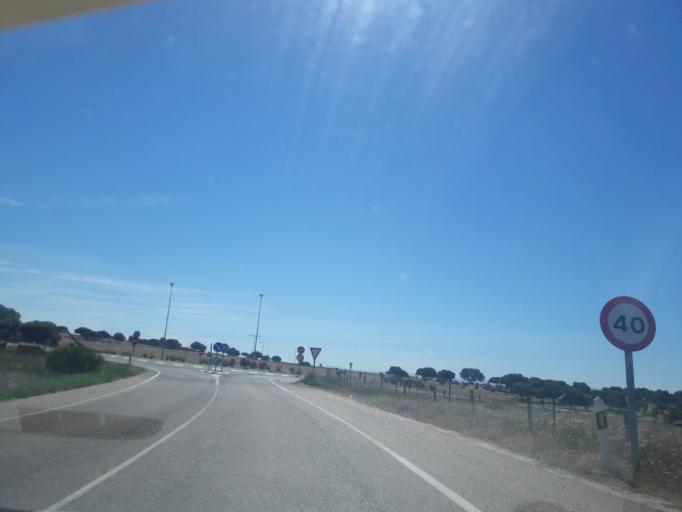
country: ES
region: Castille and Leon
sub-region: Provincia de Salamanca
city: Martinamor
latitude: 40.7991
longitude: -5.6342
